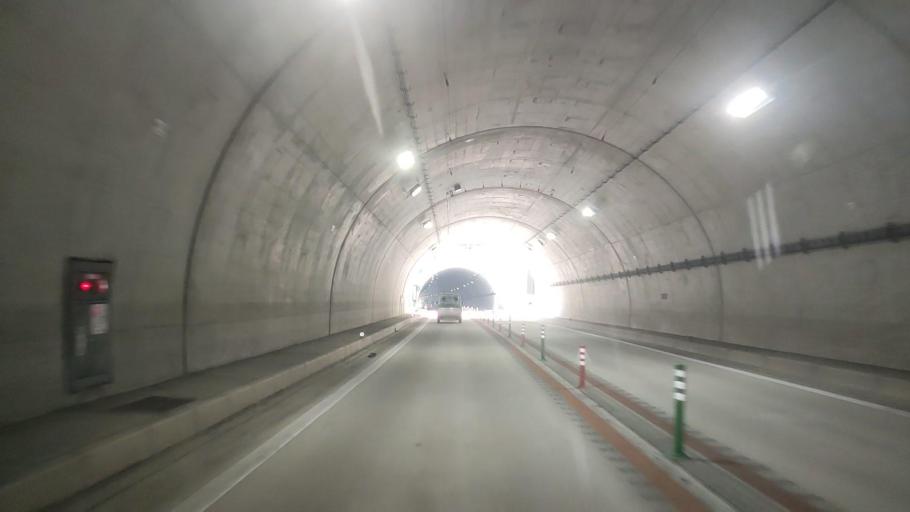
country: JP
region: Wakayama
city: Tanabe
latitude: 33.5833
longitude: 135.4509
